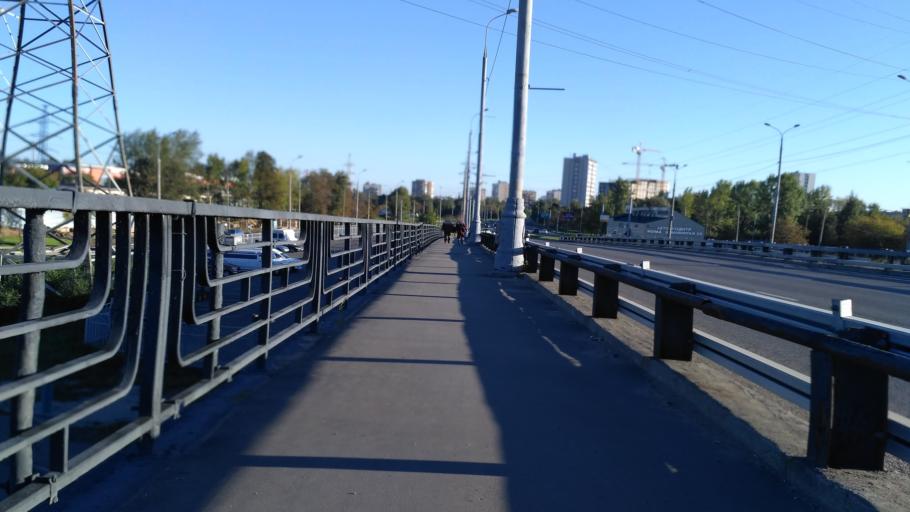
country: RU
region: Moscow
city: Novovladykino
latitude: 55.8344
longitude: 37.5781
